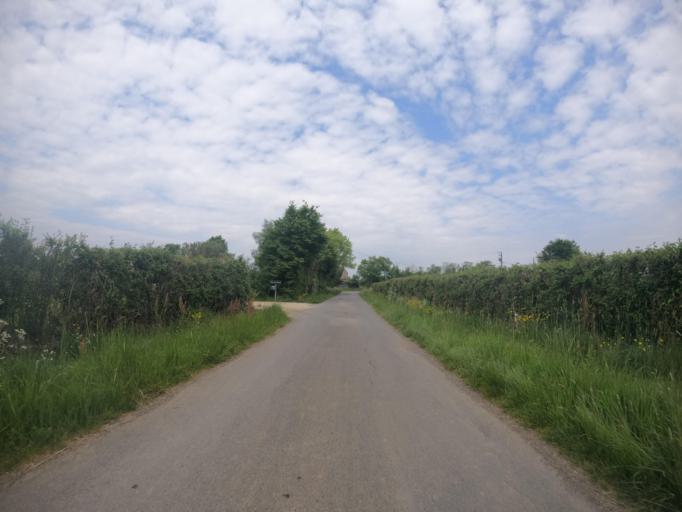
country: FR
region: Poitou-Charentes
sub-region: Departement des Deux-Sevres
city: Saint-Varent
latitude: 46.8702
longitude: -0.2804
